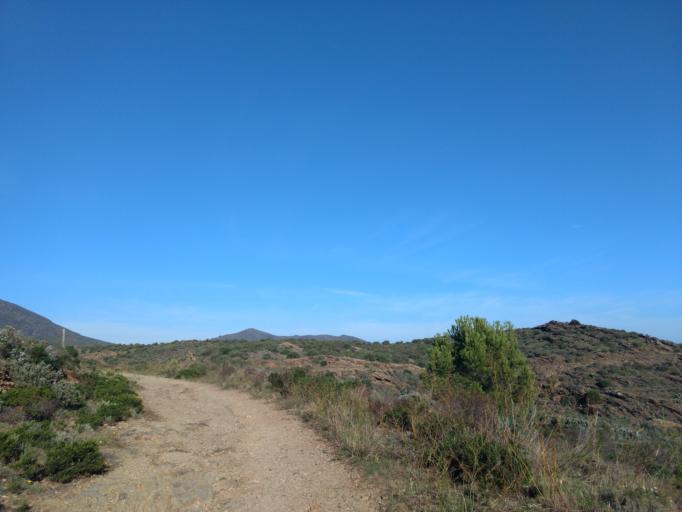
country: ES
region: Catalonia
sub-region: Provincia de Girona
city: Cadaques
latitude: 42.2731
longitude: 3.2791
